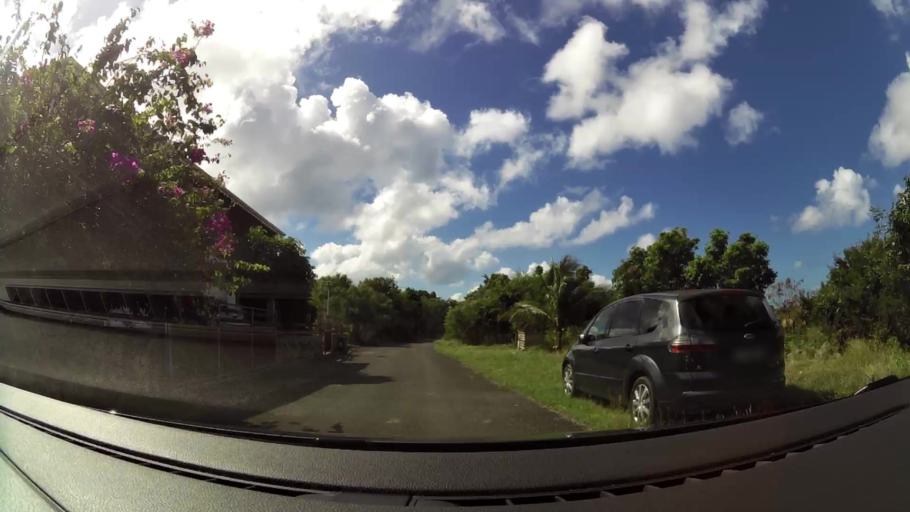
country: GP
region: Guadeloupe
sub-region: Guadeloupe
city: Port-Louis
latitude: 16.4252
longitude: -61.5239
